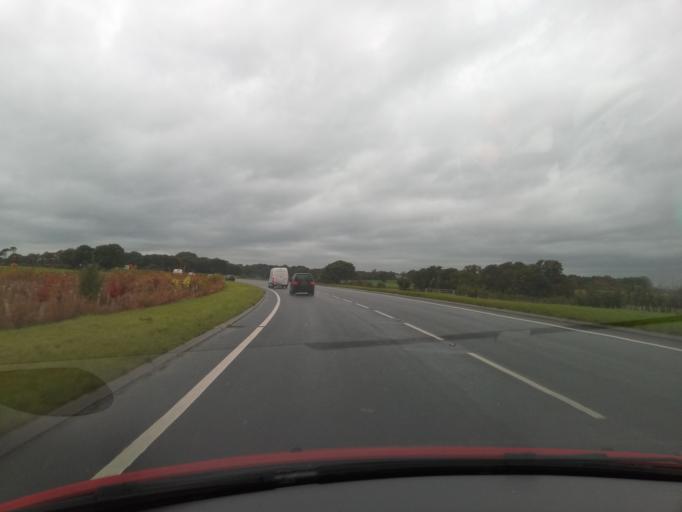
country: GB
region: England
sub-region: Lancashire
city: Preston
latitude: 53.8130
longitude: -2.7203
